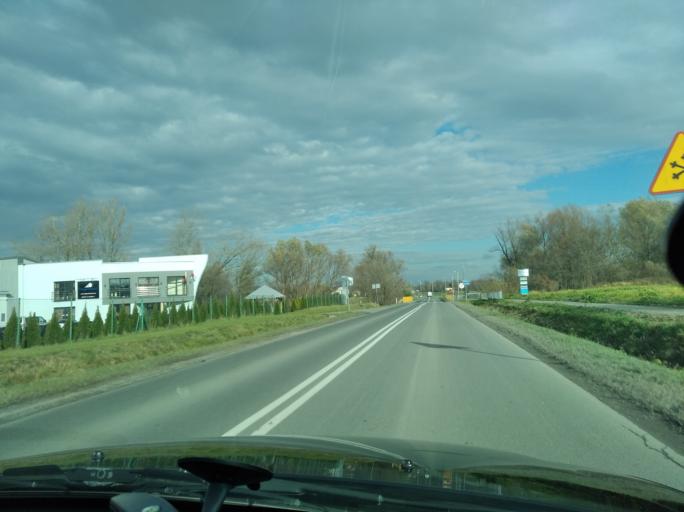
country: PL
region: Subcarpathian Voivodeship
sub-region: Powiat ropczycko-sedziszowski
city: Ostrow
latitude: 50.0881
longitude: 21.5899
